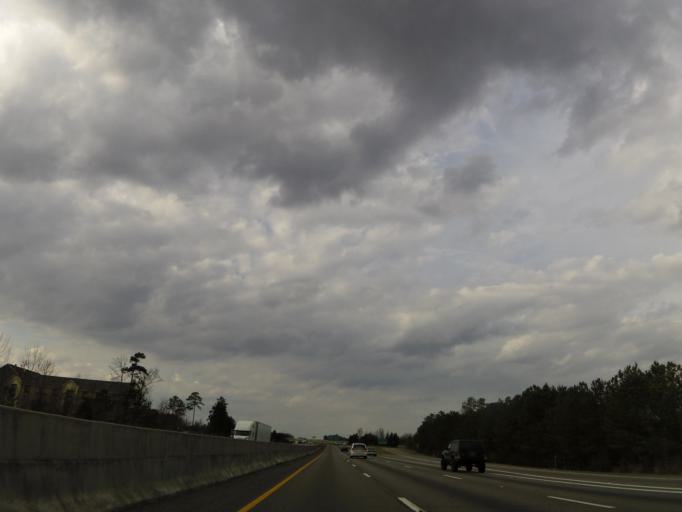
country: US
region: South Carolina
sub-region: Lexington County
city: Irmo
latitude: 34.0871
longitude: -81.1622
